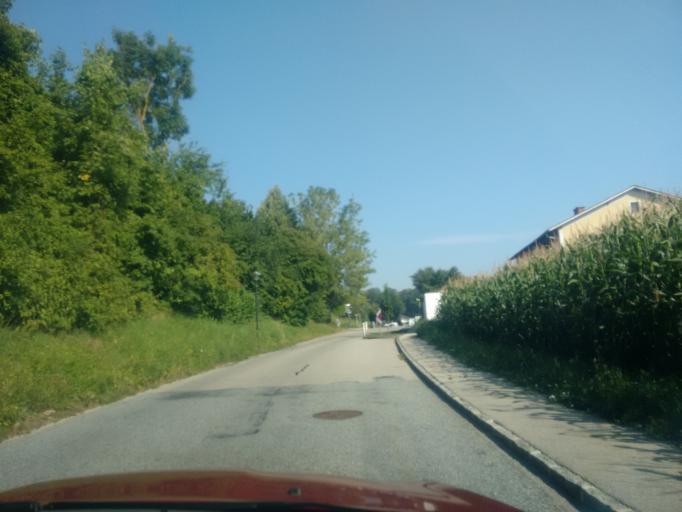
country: AT
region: Upper Austria
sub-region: Wels-Land
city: Thalheim bei Wels
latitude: 48.1473
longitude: 14.0415
